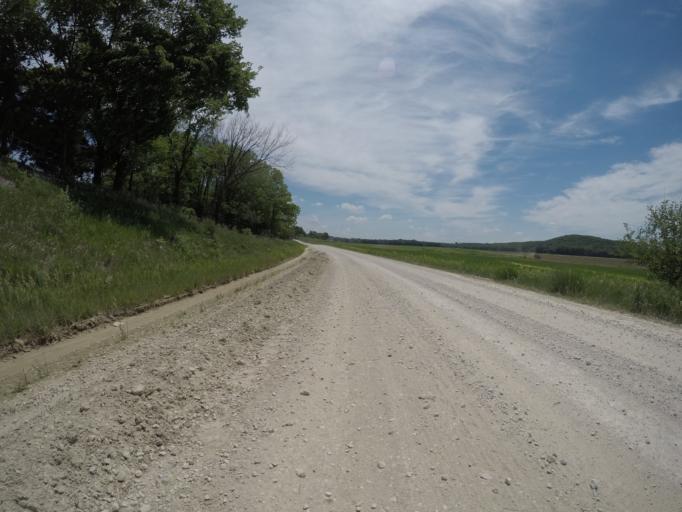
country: US
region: Kansas
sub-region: Wabaunsee County
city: Alma
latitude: 38.9688
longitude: -96.2619
